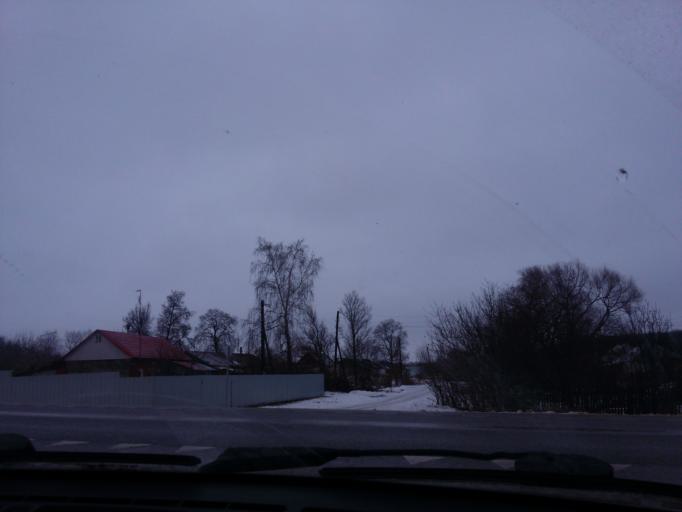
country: RU
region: Tula
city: Plavsk
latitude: 53.8139
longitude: 37.3925
